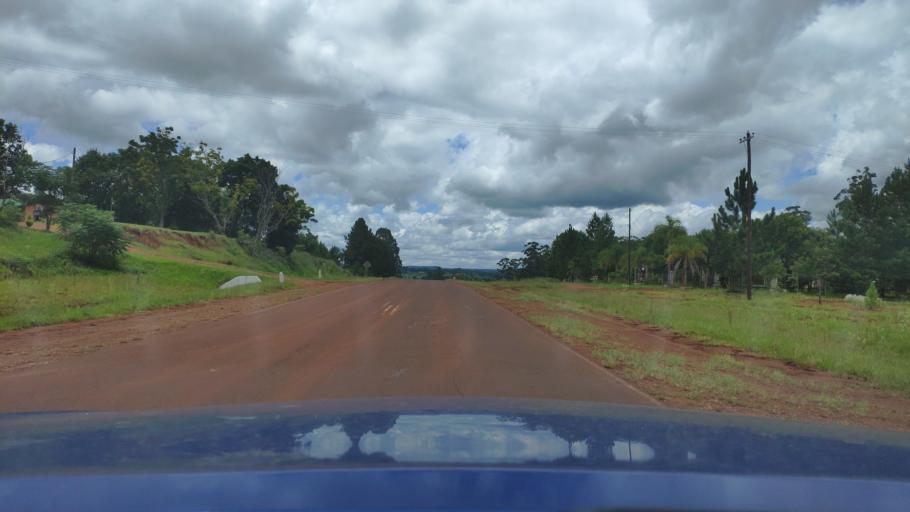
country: AR
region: Misiones
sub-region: Departamento de San Javier
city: San Javier
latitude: -27.8556
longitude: -55.2506
